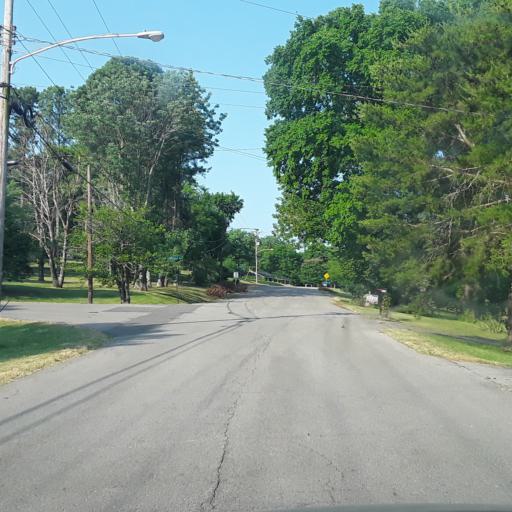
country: US
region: Tennessee
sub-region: Williamson County
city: Brentwood Estates
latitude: 36.0302
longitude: -86.7146
